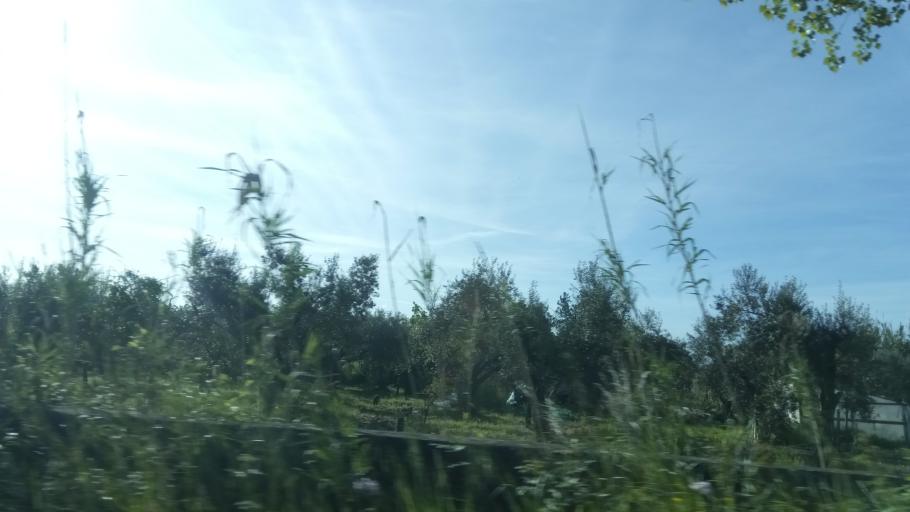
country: IT
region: Latium
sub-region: Provincia di Latina
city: Grunuovo-Campomaggiore San Luca
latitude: 41.2633
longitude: 13.7790
